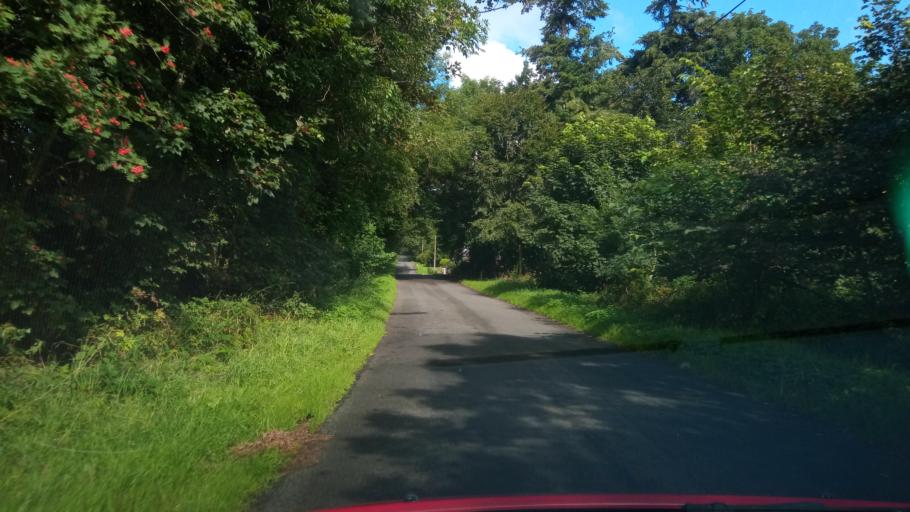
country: GB
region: Scotland
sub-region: The Scottish Borders
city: Earlston
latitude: 55.6483
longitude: -2.7001
